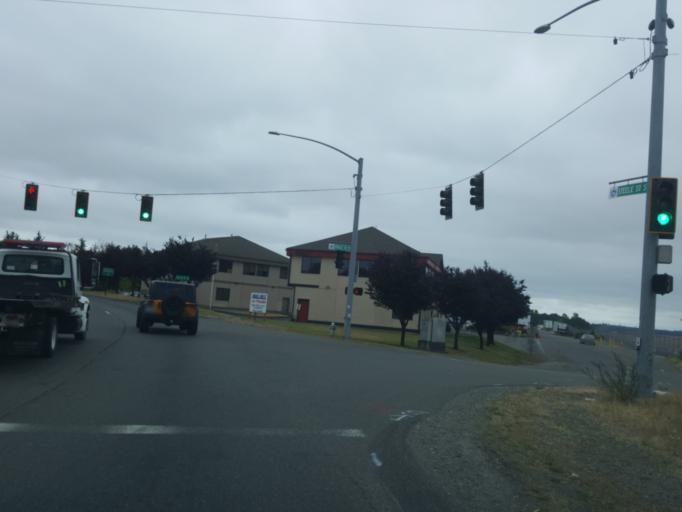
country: US
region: Washington
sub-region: Pierce County
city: McChord Air Force Base
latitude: 47.1525
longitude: -122.4680
